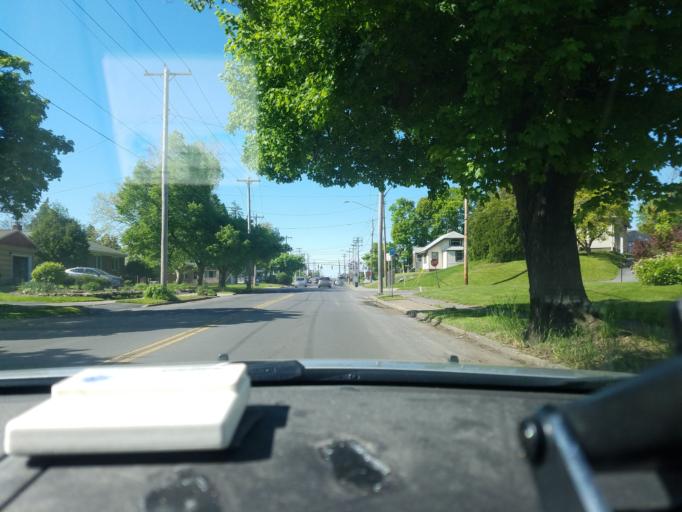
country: US
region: New York
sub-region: Onondaga County
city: Lyncourt
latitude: 43.0706
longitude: -76.1230
